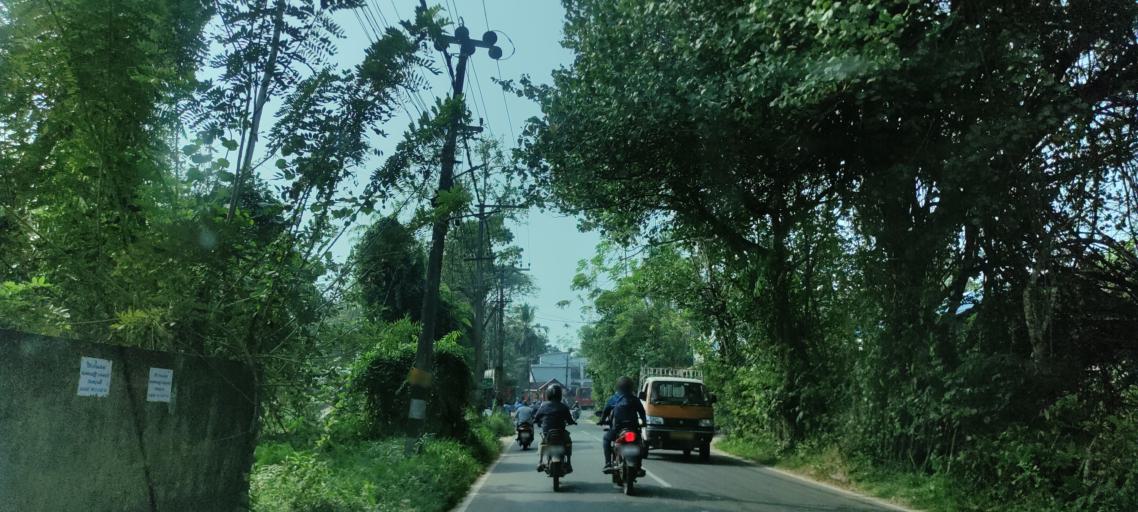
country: IN
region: Kerala
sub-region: Alappuzha
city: Vayalar
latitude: 9.6945
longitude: 76.3296
